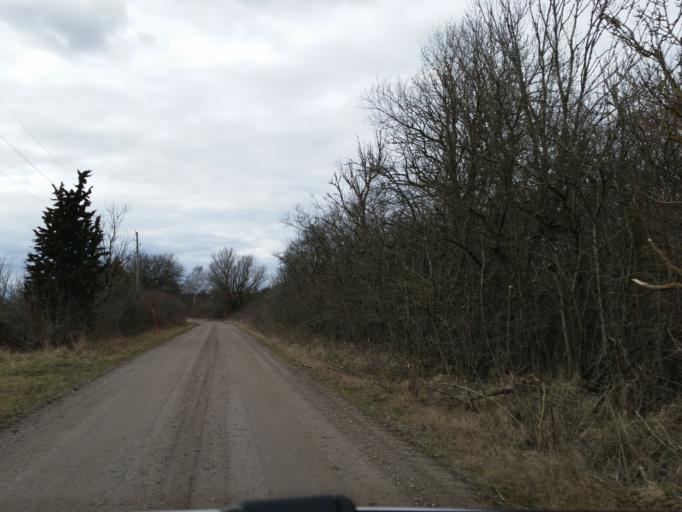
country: SE
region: Kalmar
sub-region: Morbylanga Kommun
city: Sodra Sandby
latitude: 56.6613
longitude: 16.6960
